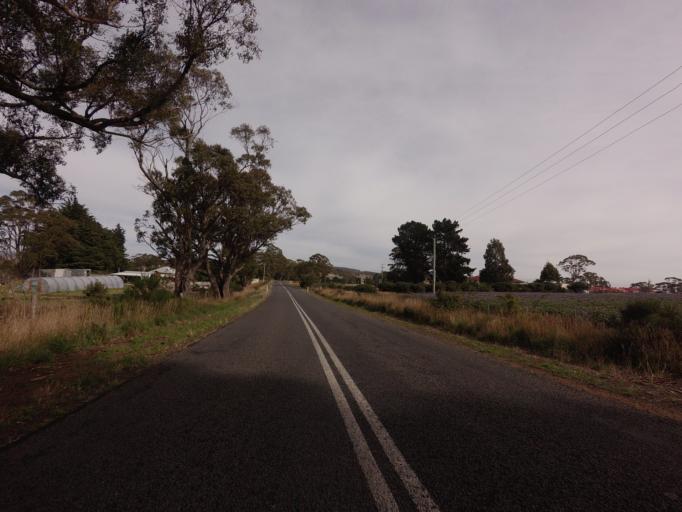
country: AU
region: Tasmania
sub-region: Brighton
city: Bridgewater
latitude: -42.3964
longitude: 147.4369
